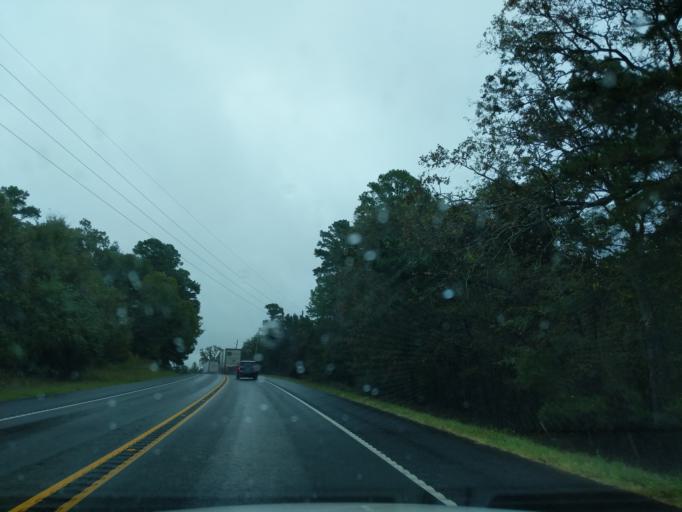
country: US
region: Louisiana
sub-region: Caddo Parish
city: Greenwood
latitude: 32.4008
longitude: -93.9996
